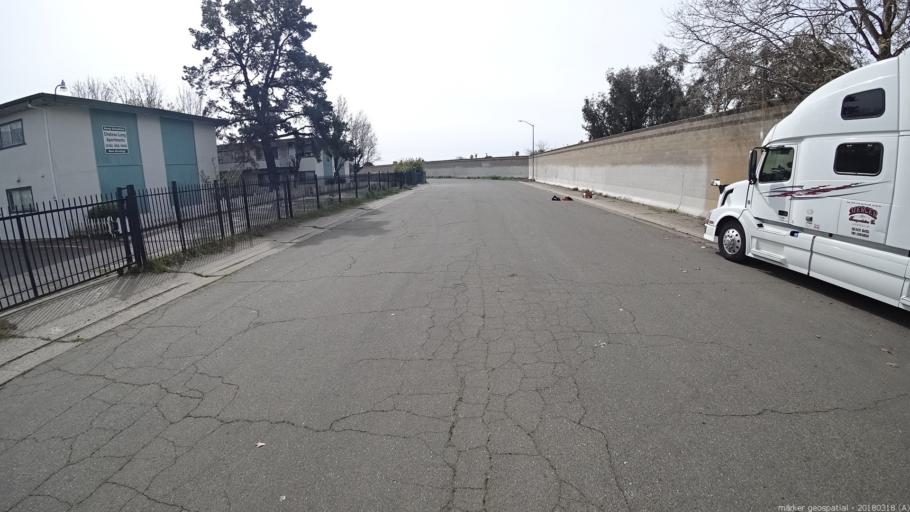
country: US
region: California
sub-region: Sacramento County
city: Parkway
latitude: 38.5059
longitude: -121.4553
